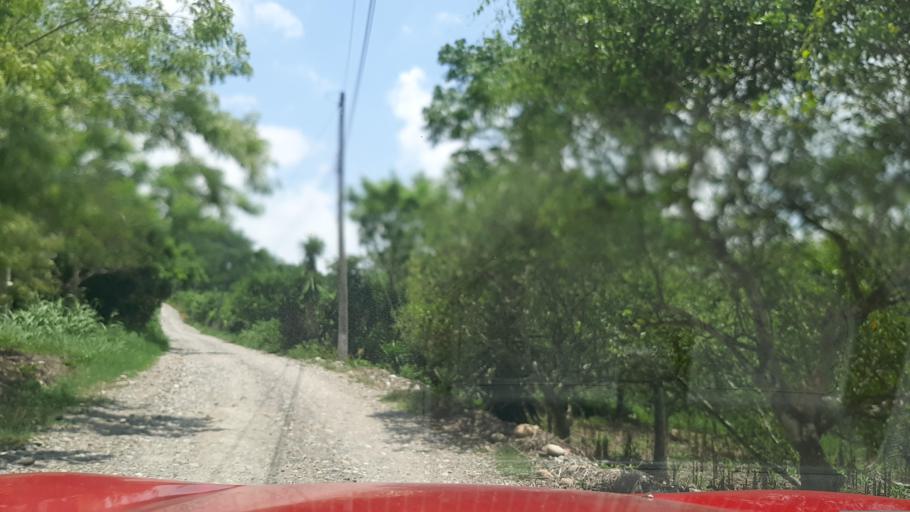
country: MX
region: Veracruz
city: Papantla de Olarte
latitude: 20.4309
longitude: -97.2646
